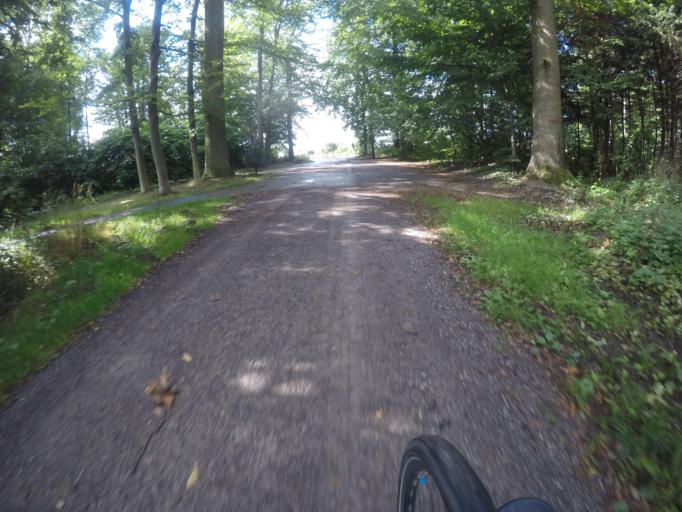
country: DE
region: Baden-Wuerttemberg
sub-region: Regierungsbezirk Stuttgart
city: Ehningen
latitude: 48.6685
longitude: 8.9507
